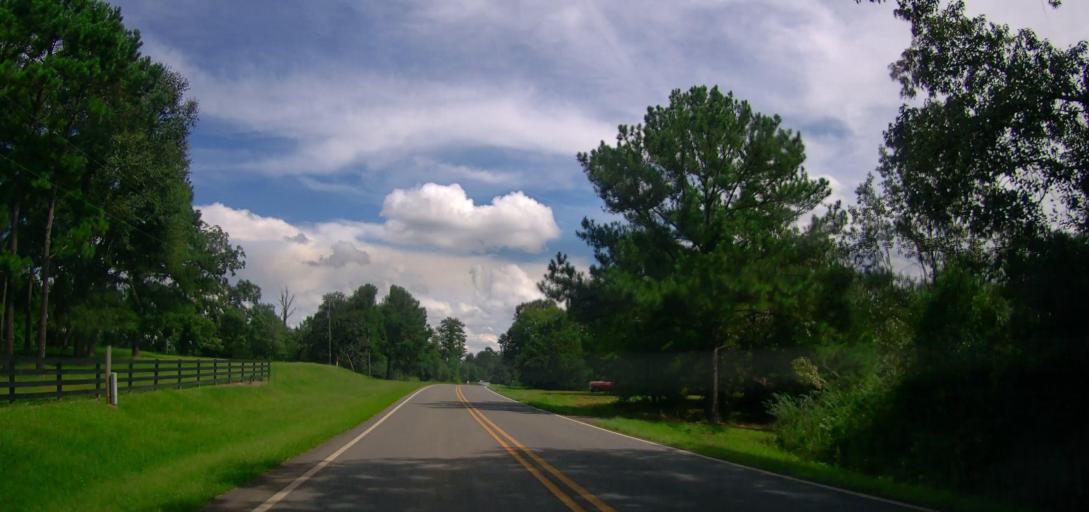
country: US
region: Georgia
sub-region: Taylor County
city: Butler
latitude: 32.5333
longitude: -84.2124
